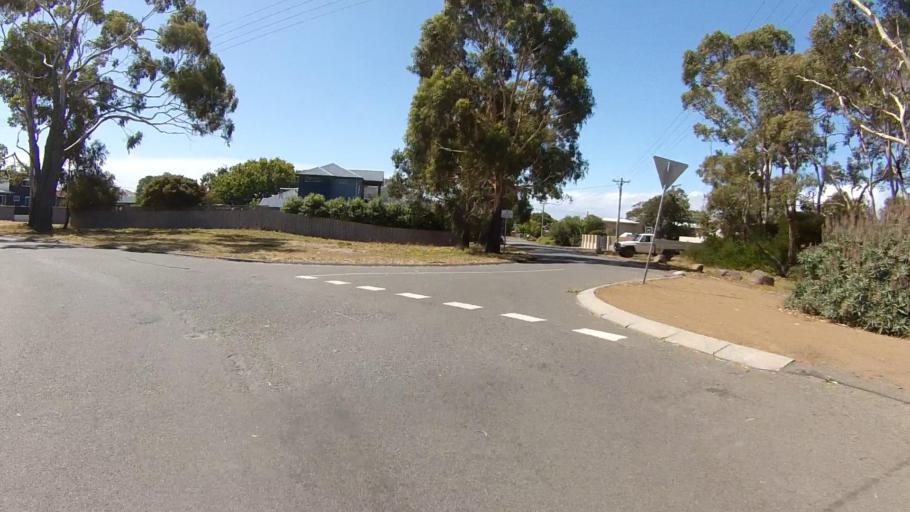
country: AU
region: Tasmania
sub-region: Clarence
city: Lauderdale
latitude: -42.8977
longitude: 147.4974
